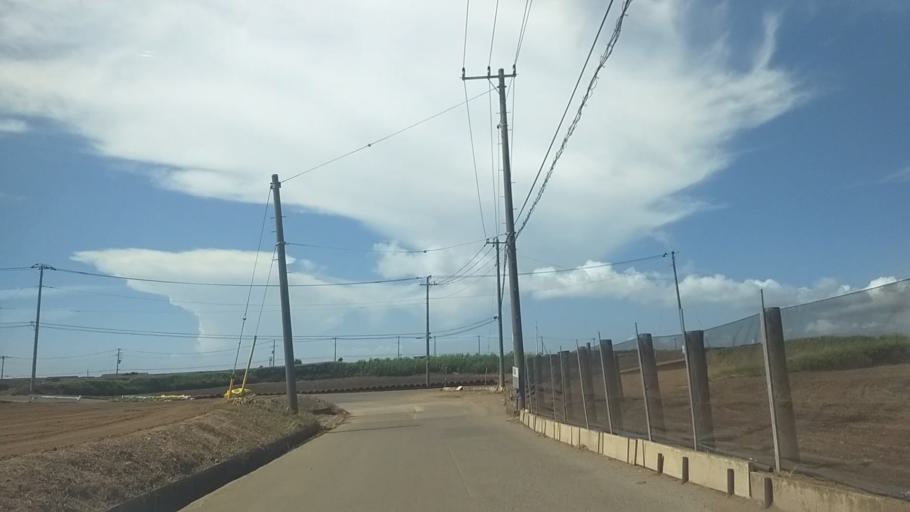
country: JP
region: Kanagawa
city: Miura
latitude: 35.1442
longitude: 139.6412
